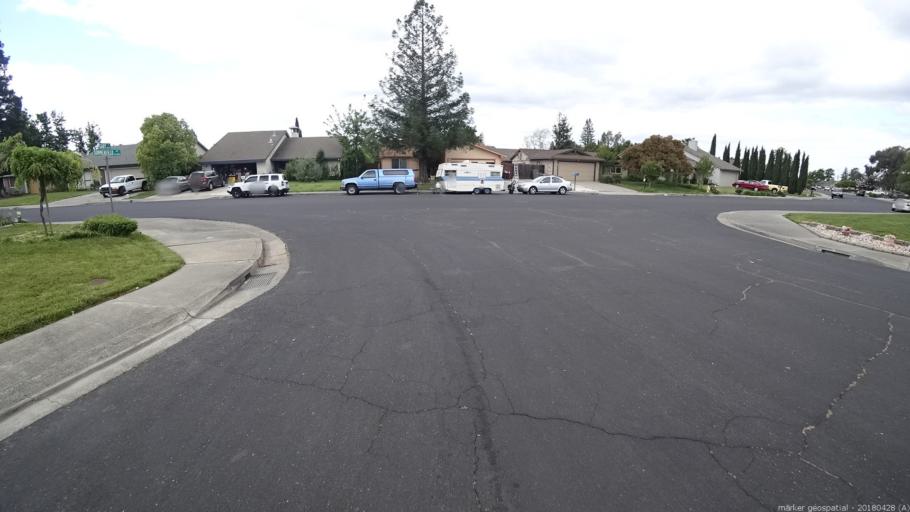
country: US
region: California
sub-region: Yolo County
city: West Sacramento
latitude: 38.5518
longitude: -121.5543
